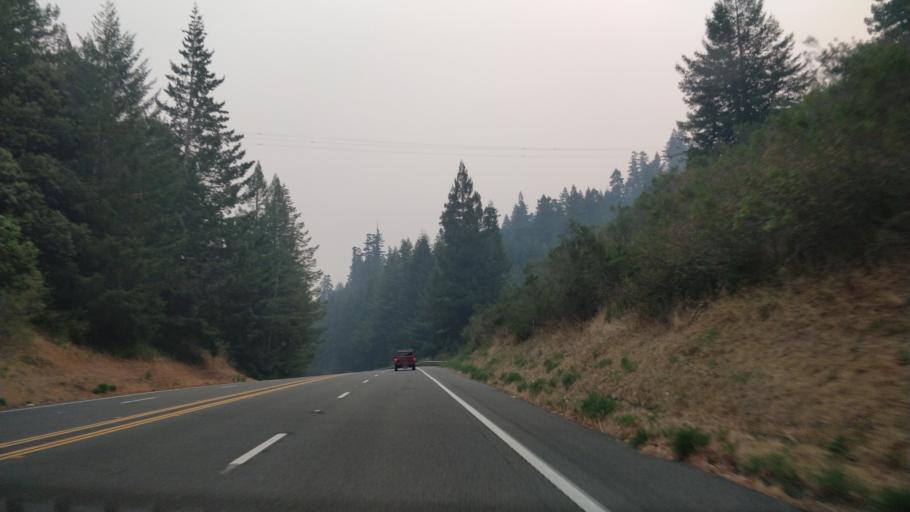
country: US
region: California
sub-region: Humboldt County
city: Rio Dell
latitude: 40.3792
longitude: -123.9281
